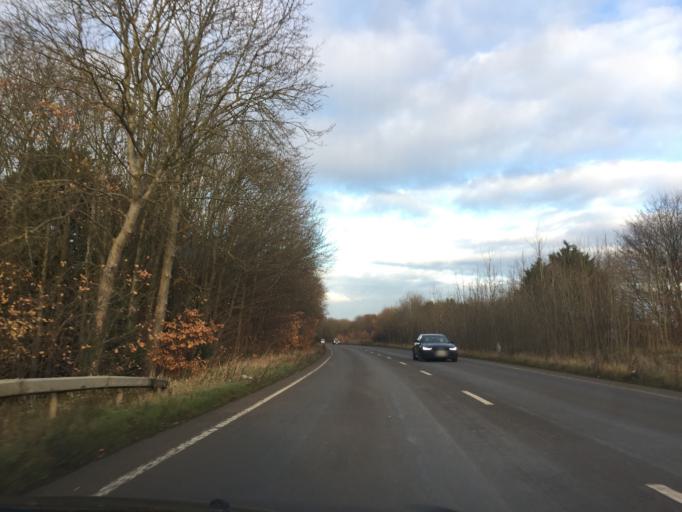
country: GB
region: England
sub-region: Northamptonshire
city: Northampton
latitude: 52.2746
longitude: -0.8557
